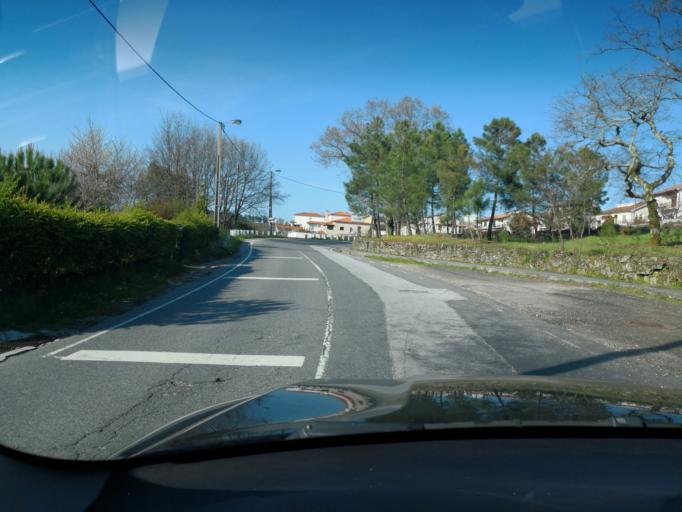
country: PT
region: Vila Real
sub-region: Vila Real
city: Vila Real
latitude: 41.3177
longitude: -7.7008
